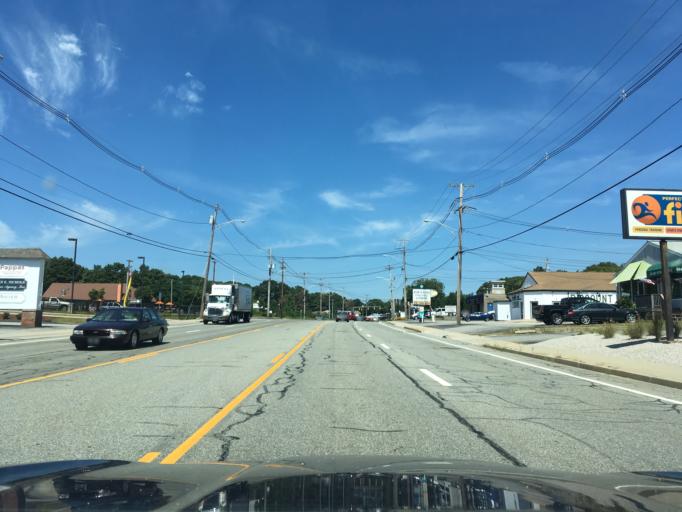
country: US
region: Rhode Island
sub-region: Kent County
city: East Greenwich
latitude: 41.6375
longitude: -71.4685
